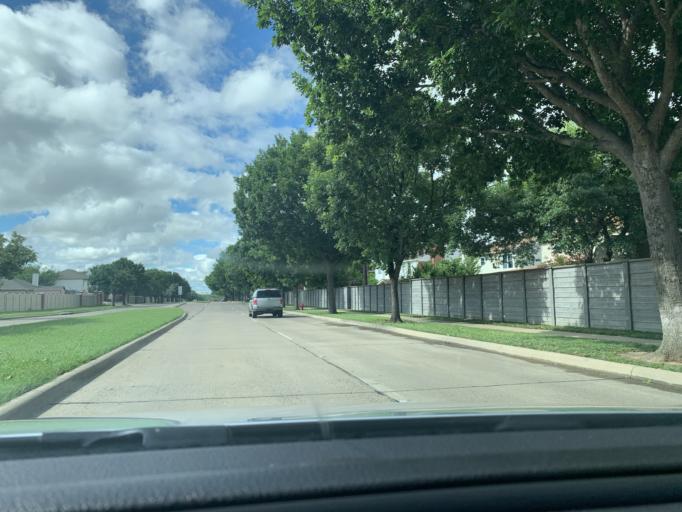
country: US
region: Texas
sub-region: Dallas County
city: Grand Prairie
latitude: 32.6634
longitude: -97.0153
